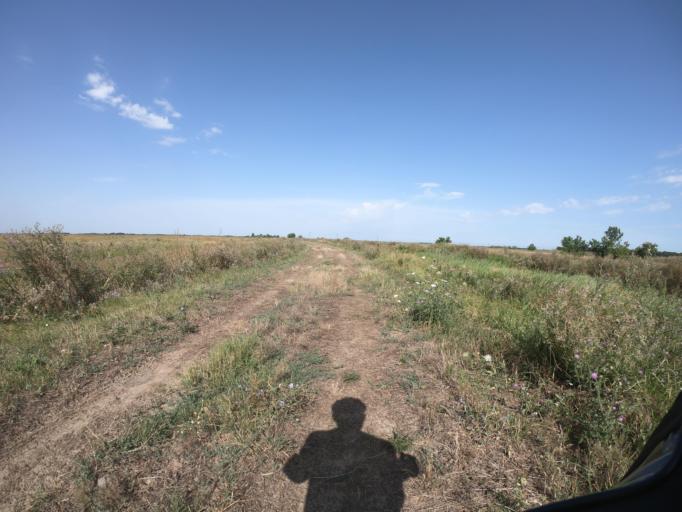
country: HU
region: Hajdu-Bihar
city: Egyek
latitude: 47.5789
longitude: 20.9222
